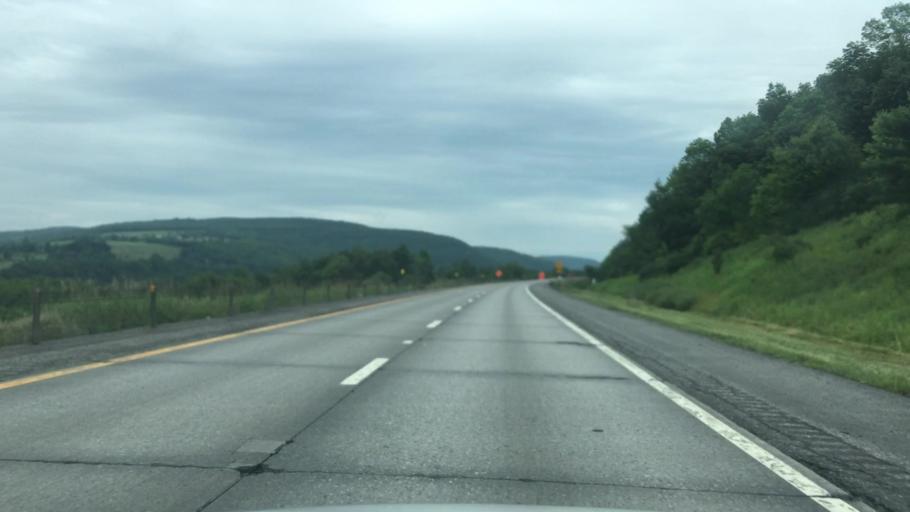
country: US
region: New York
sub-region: Otsego County
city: Worcester
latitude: 42.5251
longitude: -74.8923
